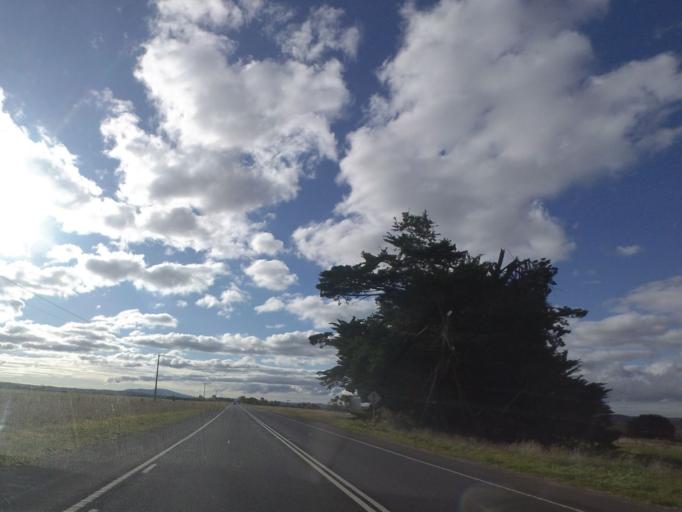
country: AU
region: Victoria
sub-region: Mount Alexander
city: Castlemaine
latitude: -37.1720
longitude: 144.3586
